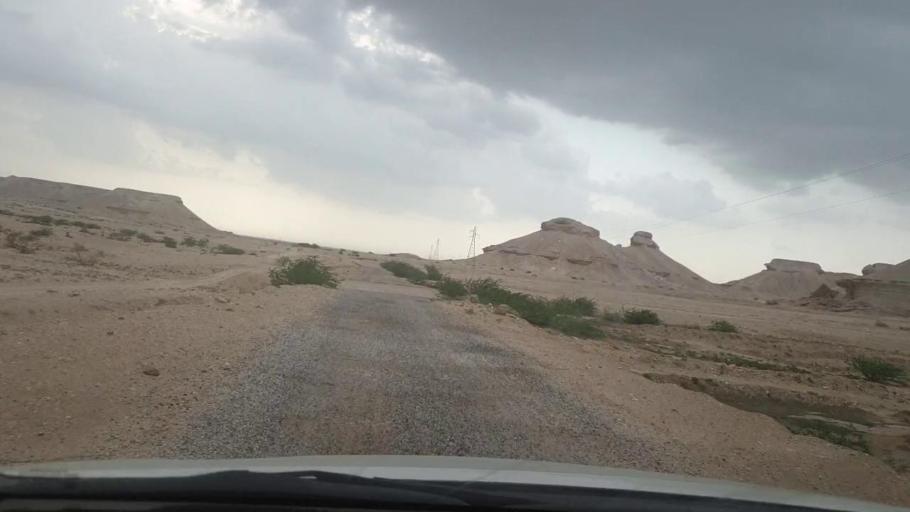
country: PK
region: Sindh
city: Khairpur
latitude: 27.4706
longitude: 68.8940
